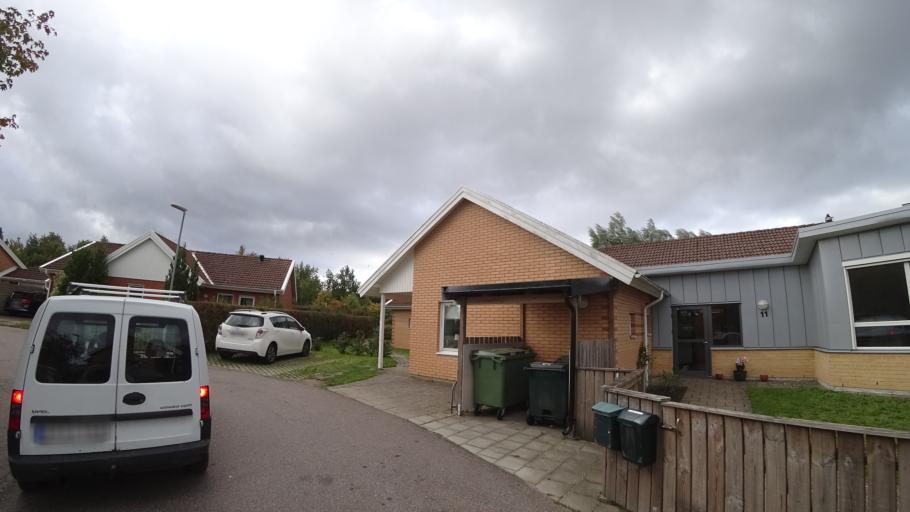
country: SE
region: Skane
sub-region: Kavlinge Kommun
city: Loddekopinge
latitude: 55.7613
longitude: 13.0228
